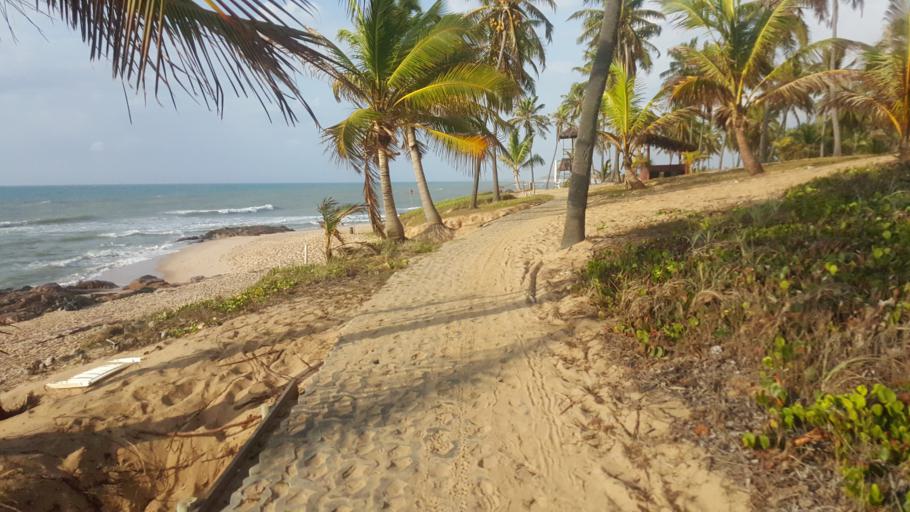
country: BR
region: Bahia
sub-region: Mata De Sao Joao
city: Mata de Sao Joao
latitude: -12.4400
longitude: -37.9168
